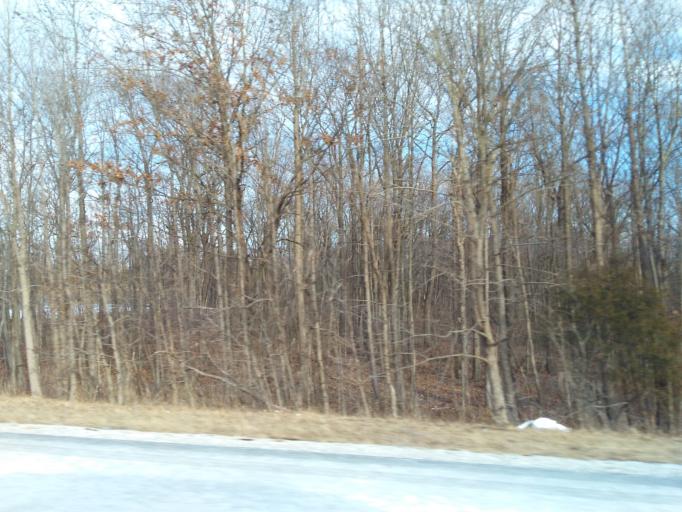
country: US
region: Illinois
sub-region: Jefferson County
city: Mount Vernon
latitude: 38.2412
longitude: -88.9059
